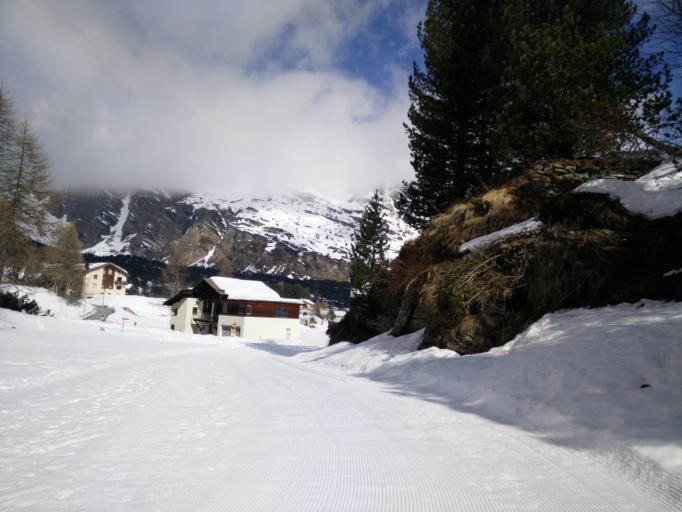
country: CH
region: Grisons
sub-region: Maloja District
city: Silvaplana
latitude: 46.4020
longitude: 9.7001
